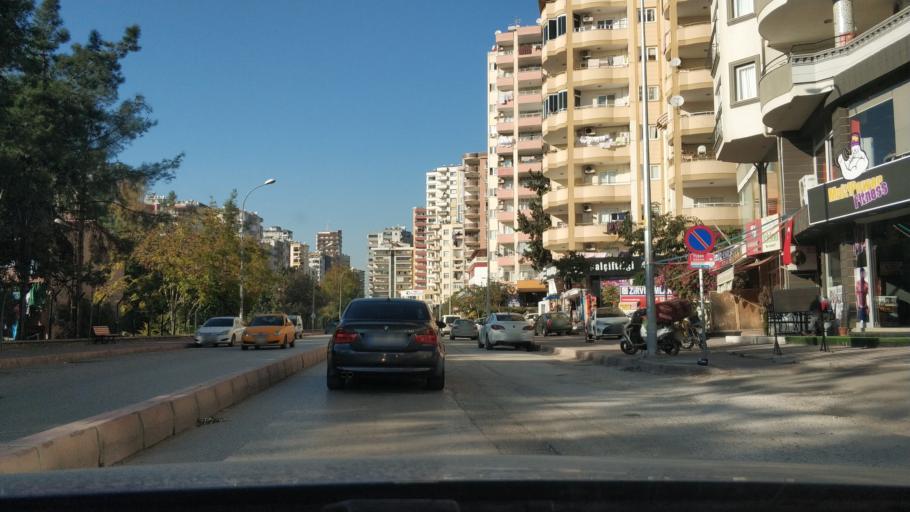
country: TR
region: Adana
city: Seyhan
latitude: 37.0502
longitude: 35.2795
